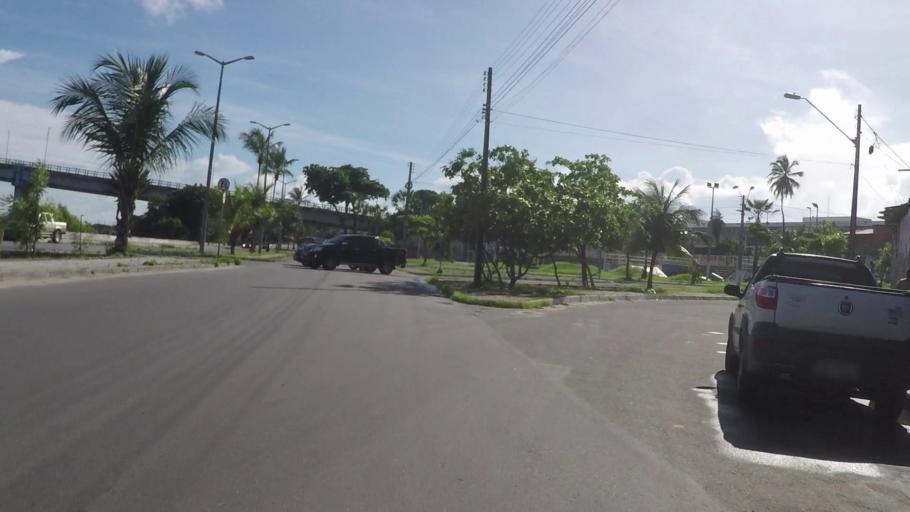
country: BR
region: Ceara
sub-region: Fortaleza
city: Fortaleza
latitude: -3.7011
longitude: -38.5892
